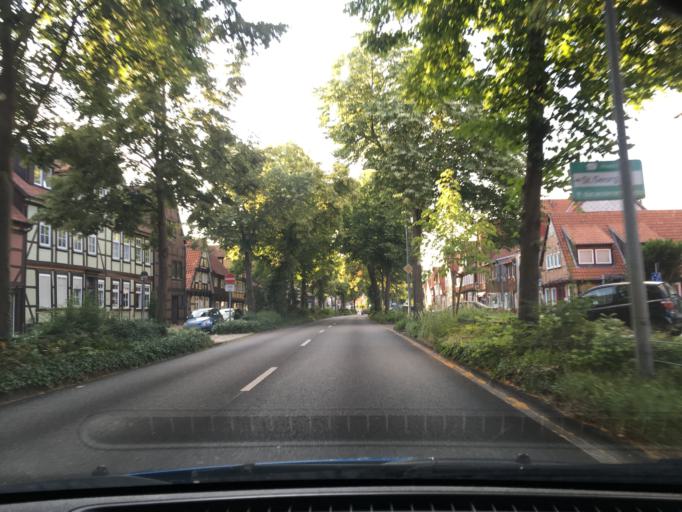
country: DE
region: Lower Saxony
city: Celle
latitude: 52.6204
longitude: 10.0909
